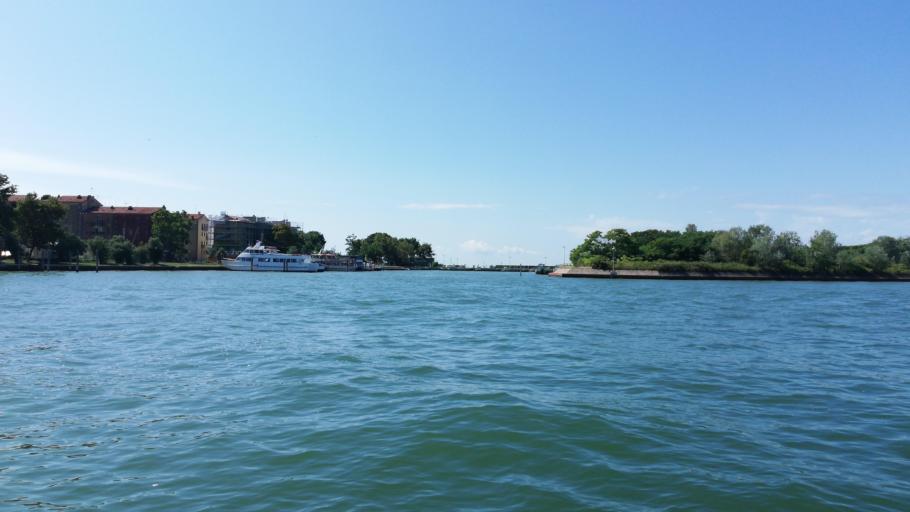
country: IT
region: Veneto
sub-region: Provincia di Venezia
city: Giudecca
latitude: 45.4295
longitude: 12.3117
